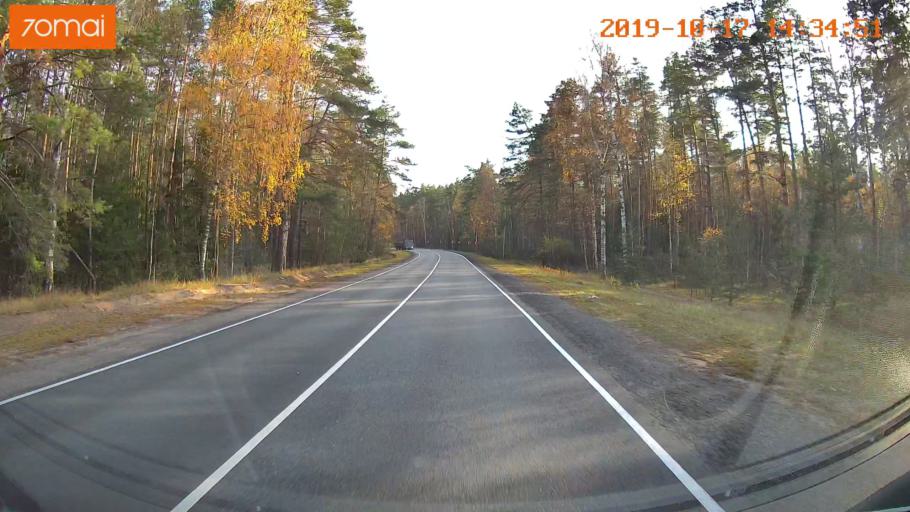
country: RU
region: Rjazan
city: Solotcha
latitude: 54.9067
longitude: 39.9997
